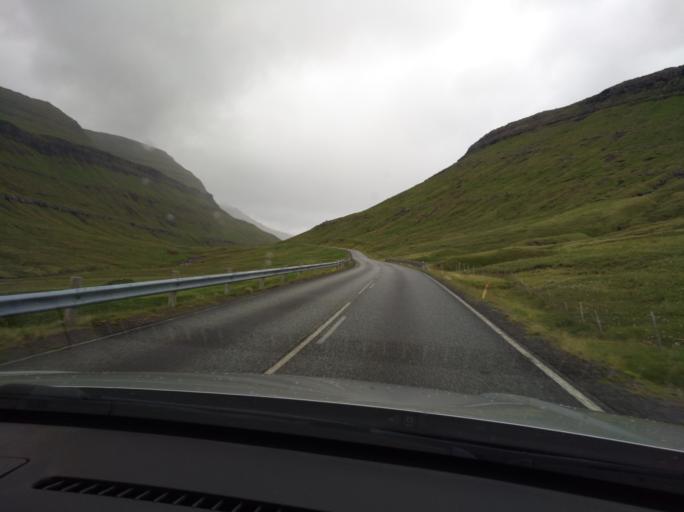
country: FO
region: Eysturoy
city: Fuglafjordur
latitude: 62.2262
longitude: -6.8794
